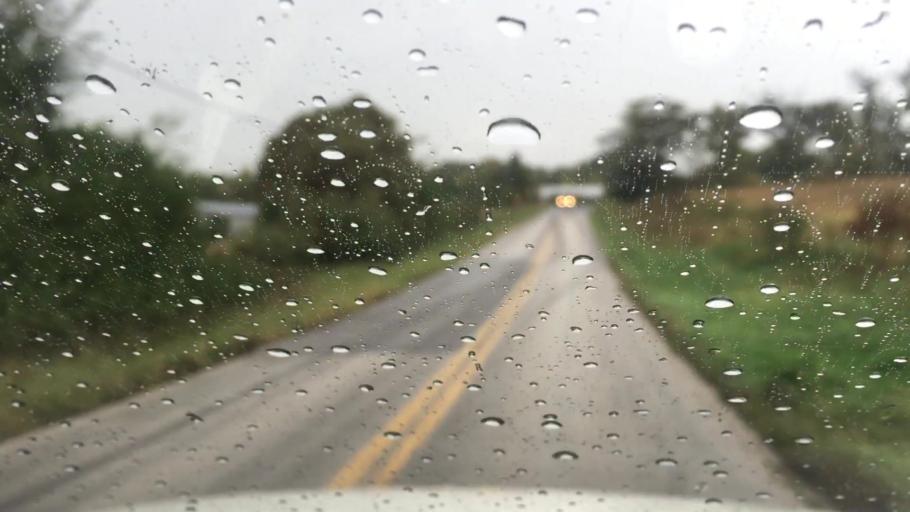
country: US
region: Missouri
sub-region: Boone County
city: Columbia
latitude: 38.9421
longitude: -92.4966
